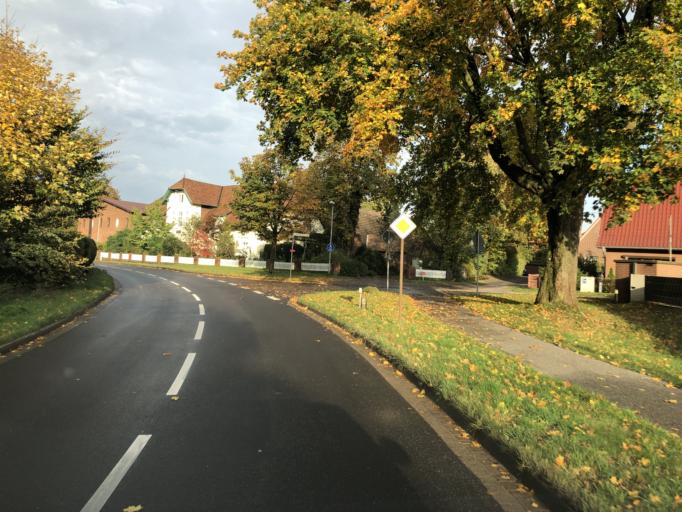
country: DE
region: Lower Saxony
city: Neu Wulmstorf
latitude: 53.4366
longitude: 9.8045
